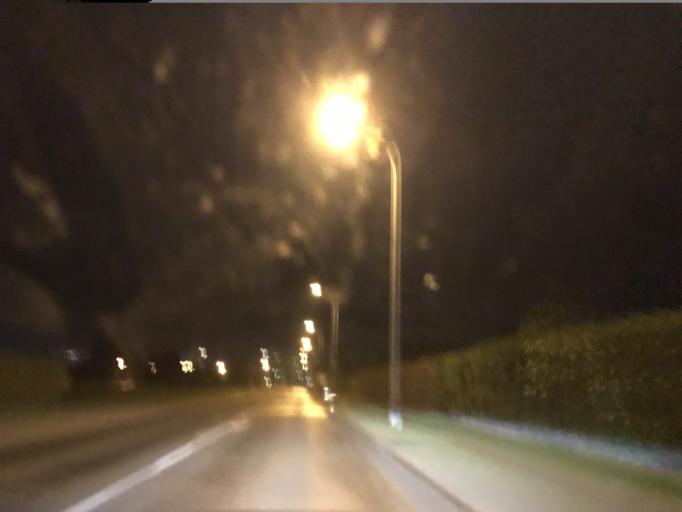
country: FR
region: Auvergne
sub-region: Departement de l'Allier
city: Vichy
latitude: 46.1111
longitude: 3.4208
